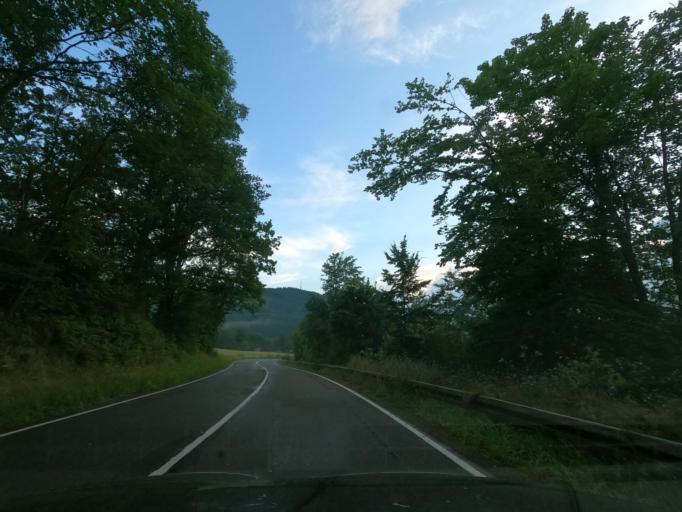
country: DE
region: North Rhine-Westphalia
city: Plettenberg
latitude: 51.2362
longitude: 7.8959
